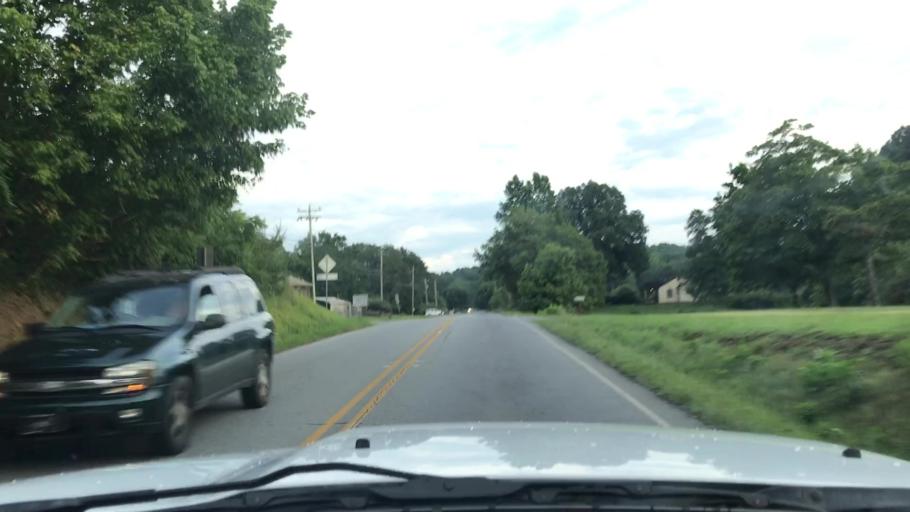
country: US
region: Georgia
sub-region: Fannin County
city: Blue Ridge
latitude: 34.9024
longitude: -84.2660
